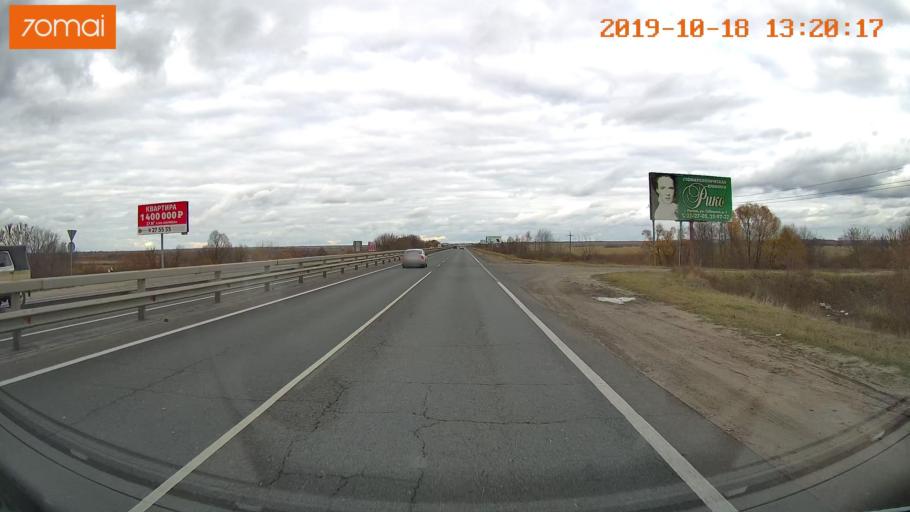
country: RU
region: Rjazan
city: Polyany
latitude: 54.6784
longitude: 39.8305
